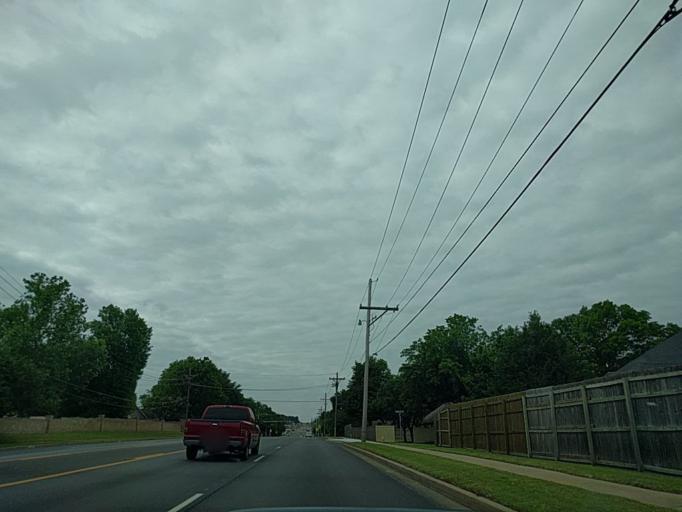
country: US
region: Oklahoma
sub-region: Tulsa County
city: Jenks
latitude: 36.0836
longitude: -95.9045
